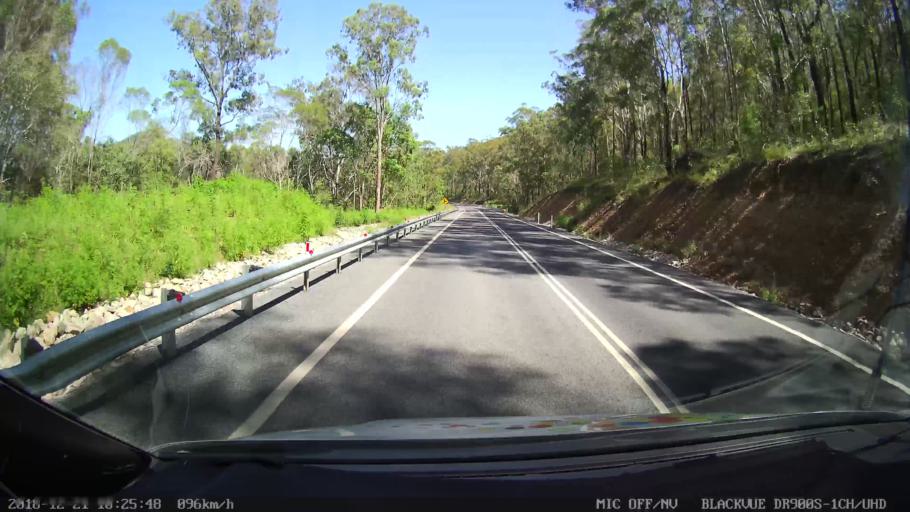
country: AU
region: New South Wales
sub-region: Clarence Valley
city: South Grafton
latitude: -29.6310
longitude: 152.7607
